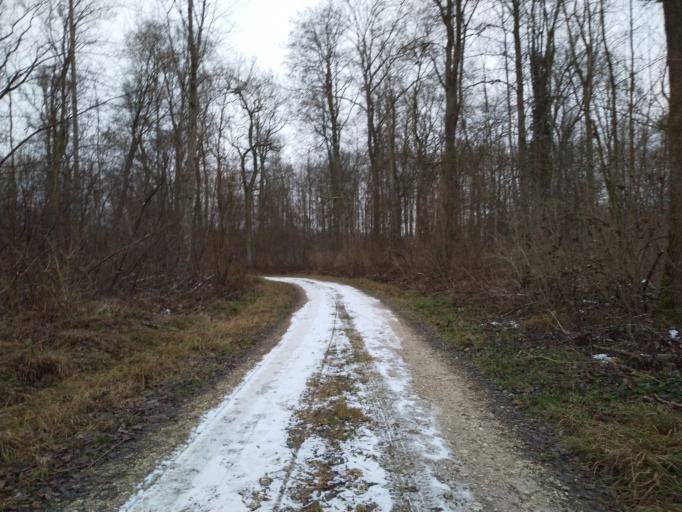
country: DE
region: Bavaria
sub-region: Swabia
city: Offingen
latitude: 48.4875
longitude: 10.3358
